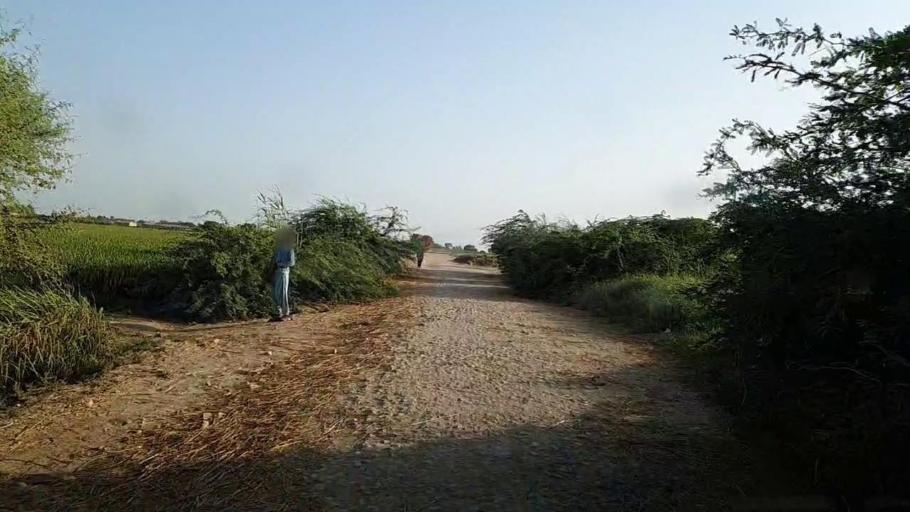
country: PK
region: Sindh
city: Bulri
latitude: 24.7447
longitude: 68.4219
